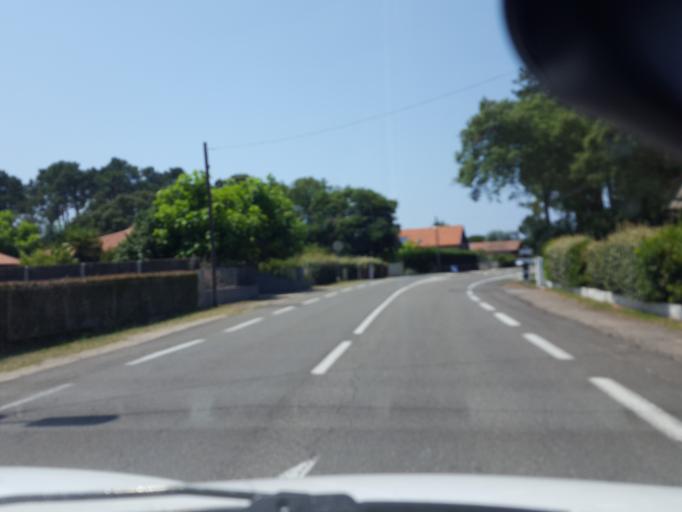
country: FR
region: Aquitaine
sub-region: Departement des Landes
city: Ondres
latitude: 43.5704
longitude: -1.4661
